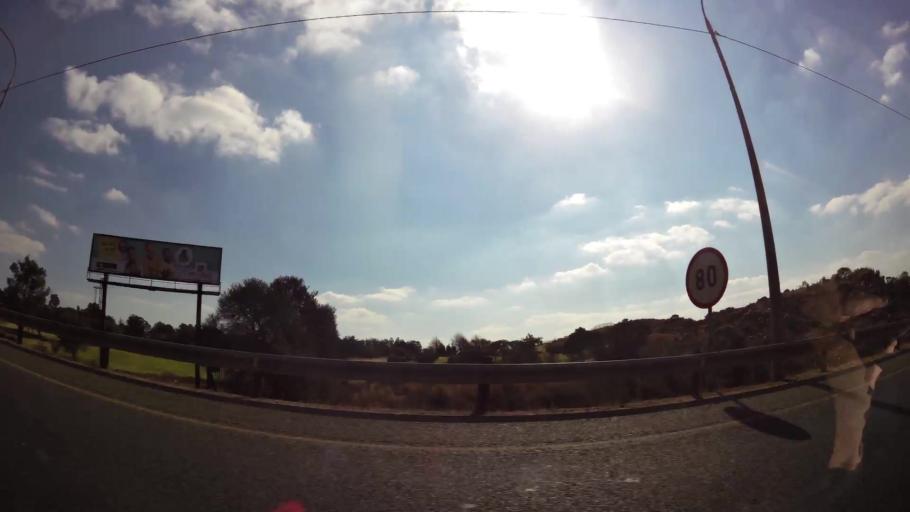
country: ZA
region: Gauteng
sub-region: West Rand District Municipality
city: Krugersdorp
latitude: -26.0788
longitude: 27.7910
